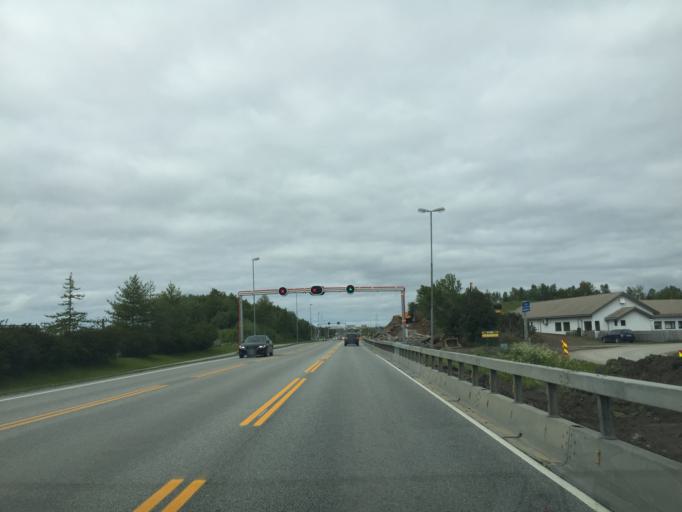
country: NO
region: Nordland
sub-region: Bodo
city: Bodo
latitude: 67.2764
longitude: 14.4390
